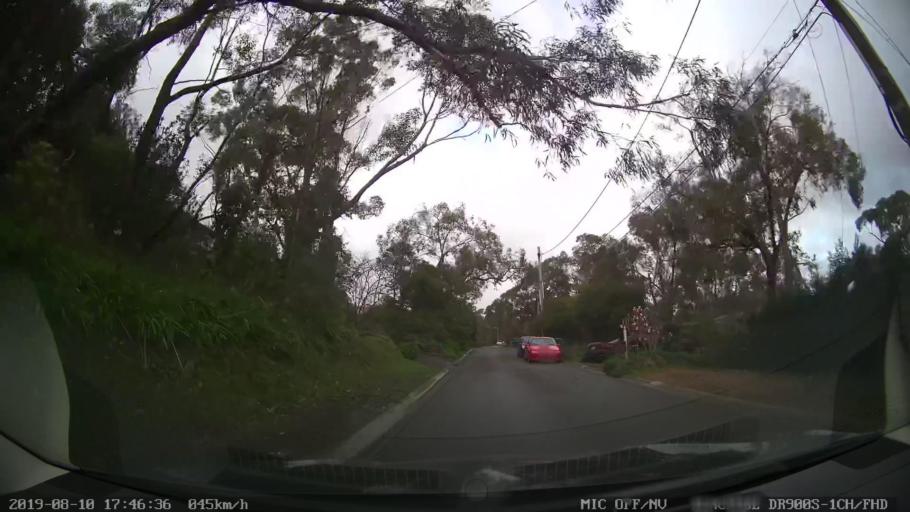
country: AU
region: Victoria
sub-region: Yarra Ranges
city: Tremont
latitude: -37.8965
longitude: 145.3211
